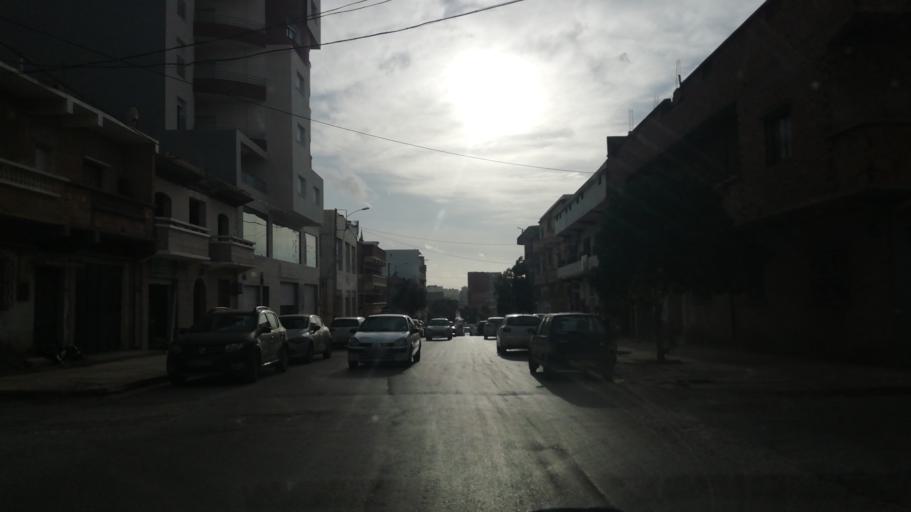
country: DZ
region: Oran
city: Bir el Djir
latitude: 35.7311
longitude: -0.5779
